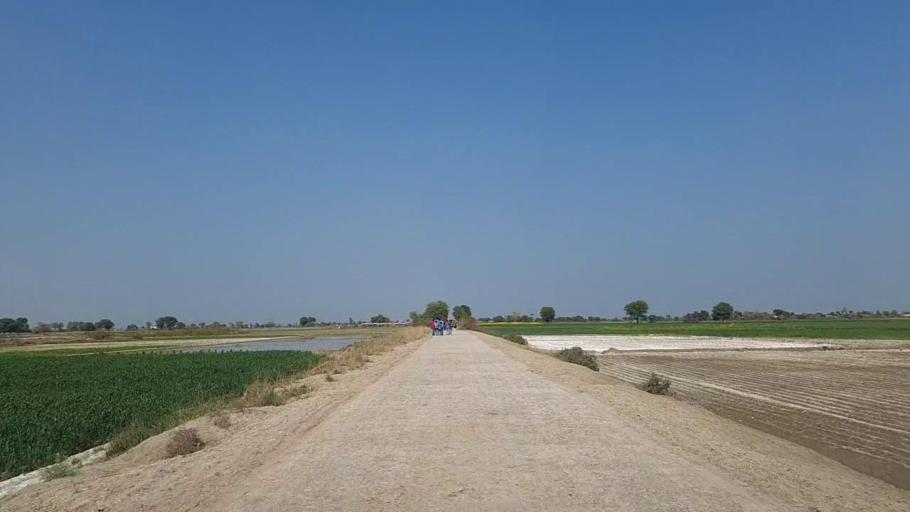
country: PK
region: Sindh
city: Nawabshah
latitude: 26.2683
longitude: 68.5133
